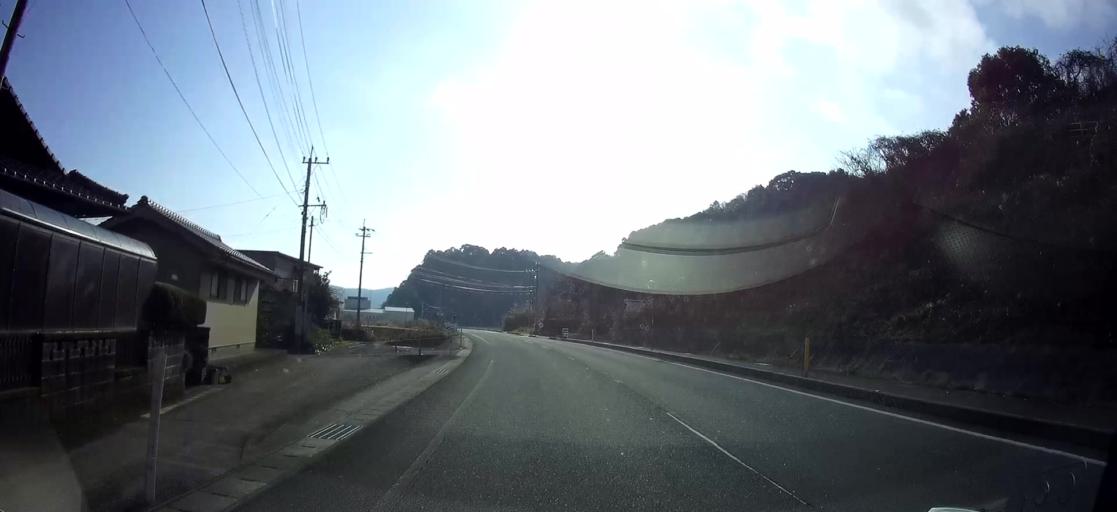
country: JP
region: Kumamoto
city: Yatsushiro
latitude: 32.4492
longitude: 130.4172
